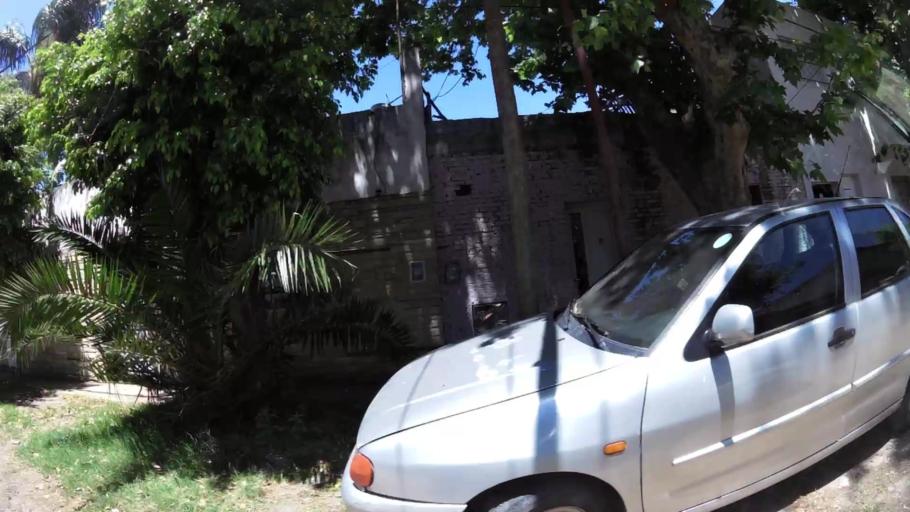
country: AR
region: Buenos Aires
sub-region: Partido de General San Martin
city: General San Martin
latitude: -34.5967
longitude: -58.5294
